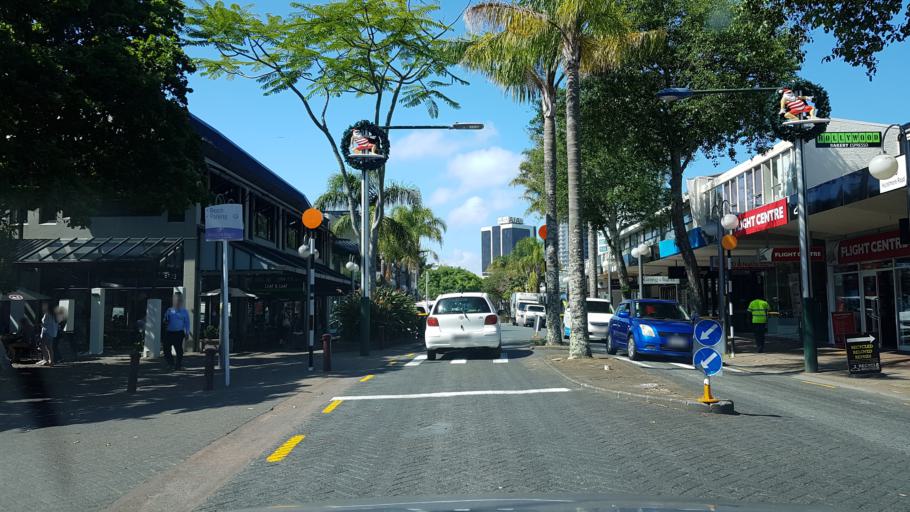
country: NZ
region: Auckland
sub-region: Auckland
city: North Shore
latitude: -36.7864
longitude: 174.7730
